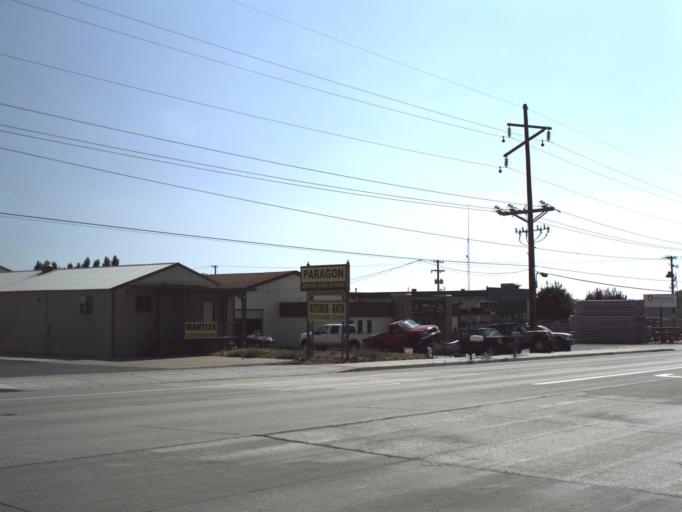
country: US
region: Utah
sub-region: Weber County
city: Ogden
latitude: 41.2445
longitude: -111.9938
